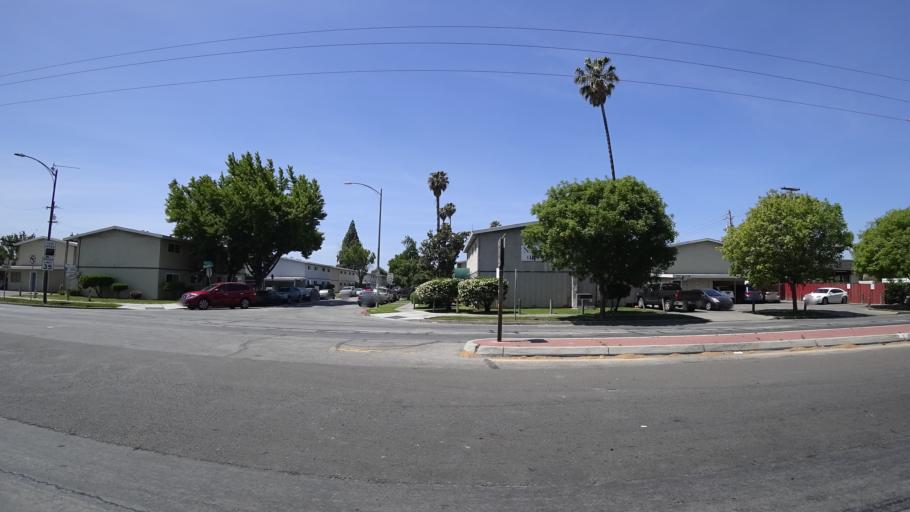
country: US
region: California
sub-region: Santa Clara County
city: Alum Rock
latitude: 37.3316
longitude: -121.8525
